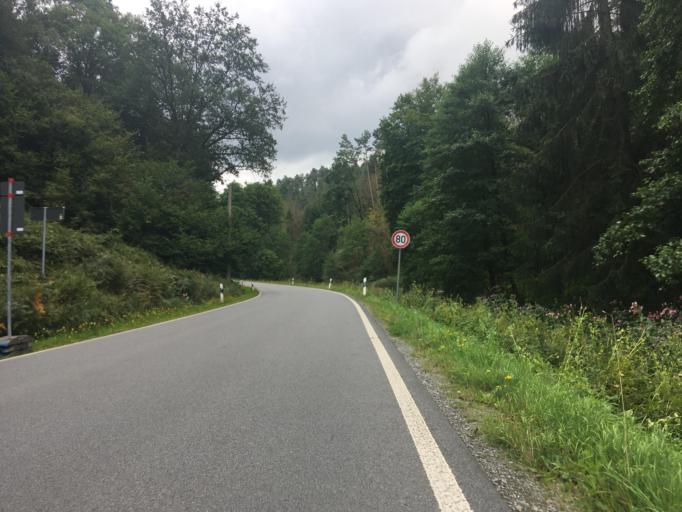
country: CZ
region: Ustecky
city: Mikulasovice
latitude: 50.9287
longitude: 14.3269
